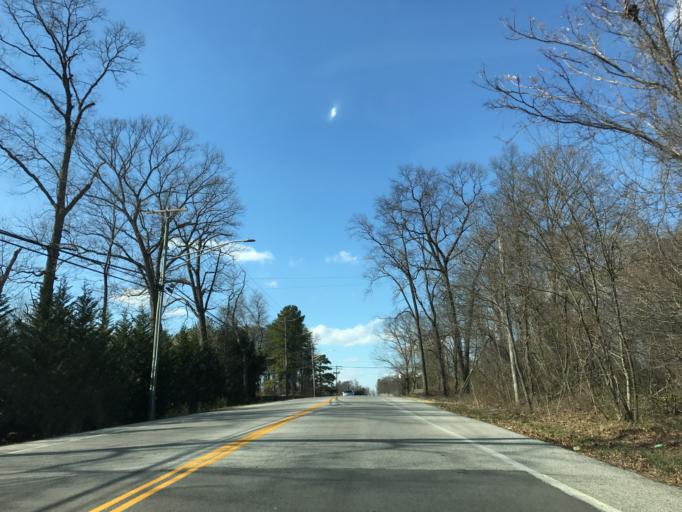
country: US
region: Maryland
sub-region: Anne Arundel County
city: Pasadena
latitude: 39.1082
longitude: -76.5835
